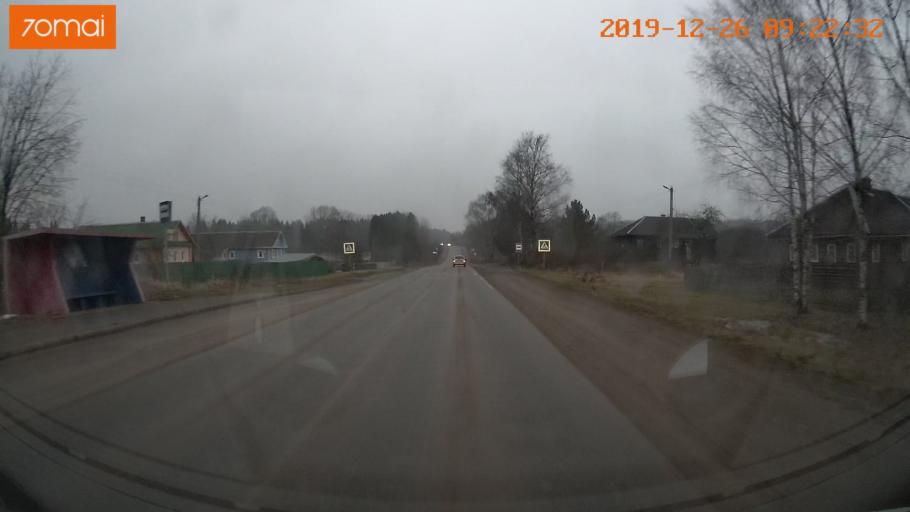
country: RU
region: Vologda
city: Gryazovets
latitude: 58.9818
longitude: 40.2150
